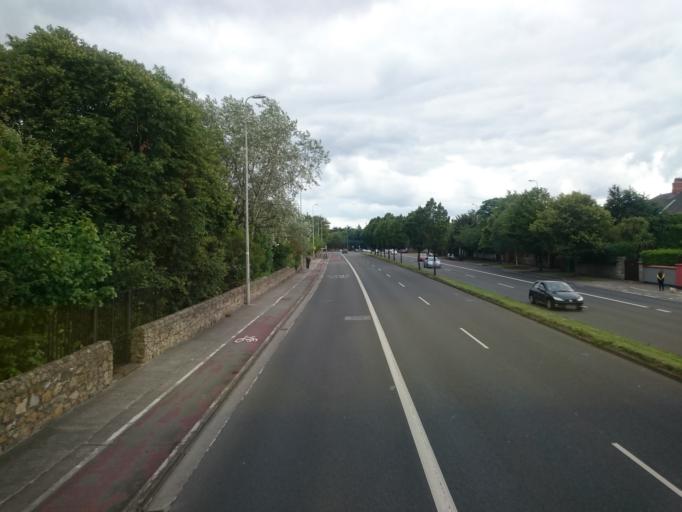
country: IE
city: Clonskeagh
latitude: 53.3169
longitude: -6.2286
